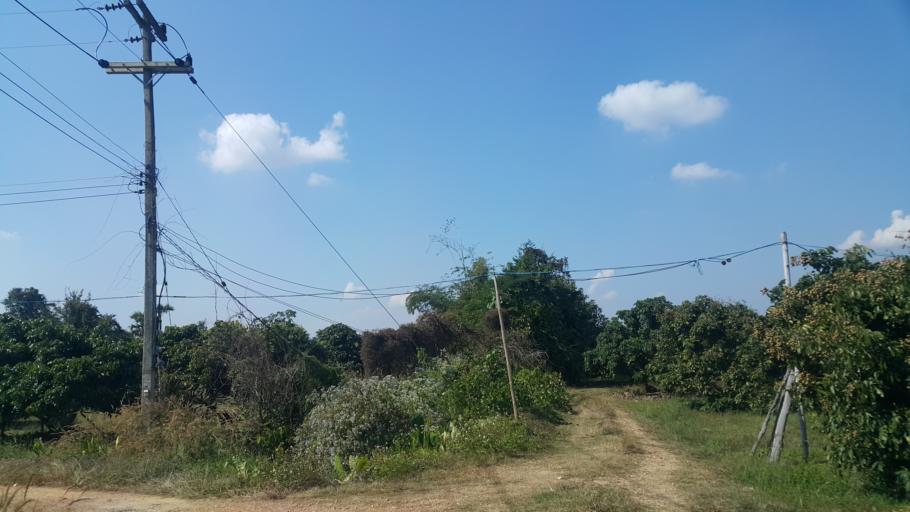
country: TH
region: Lamphun
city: Ban Thi
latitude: 18.6300
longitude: 99.1565
